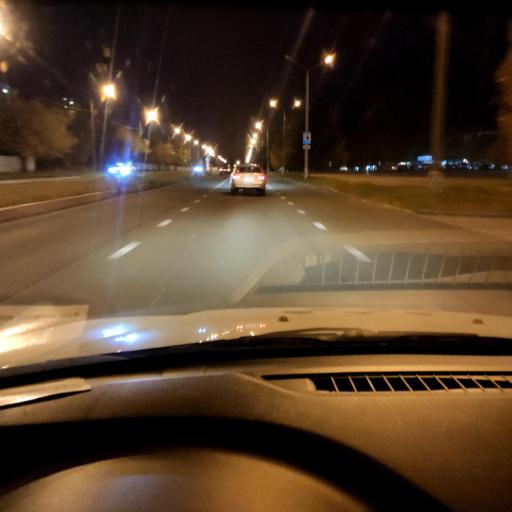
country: RU
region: Samara
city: Tol'yatti
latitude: 53.5057
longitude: 49.2703
